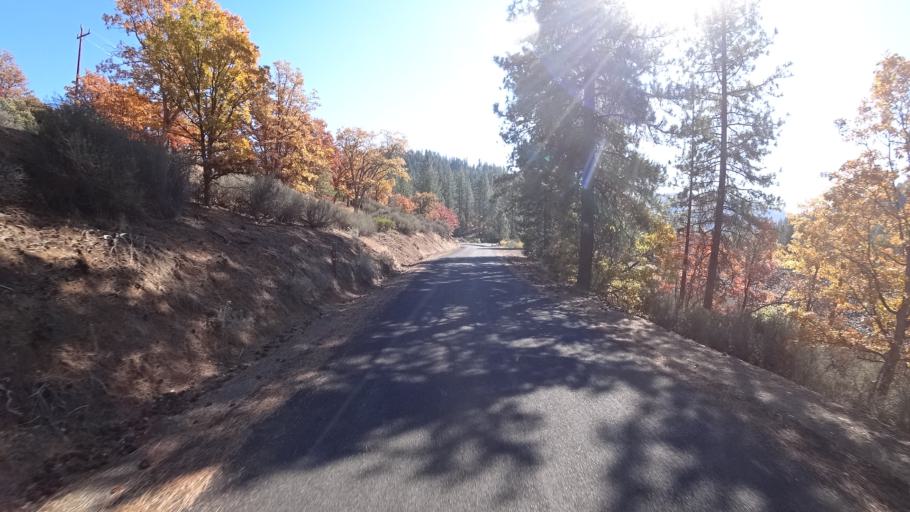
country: US
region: California
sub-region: Siskiyou County
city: Yreka
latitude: 41.6799
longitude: -122.8495
